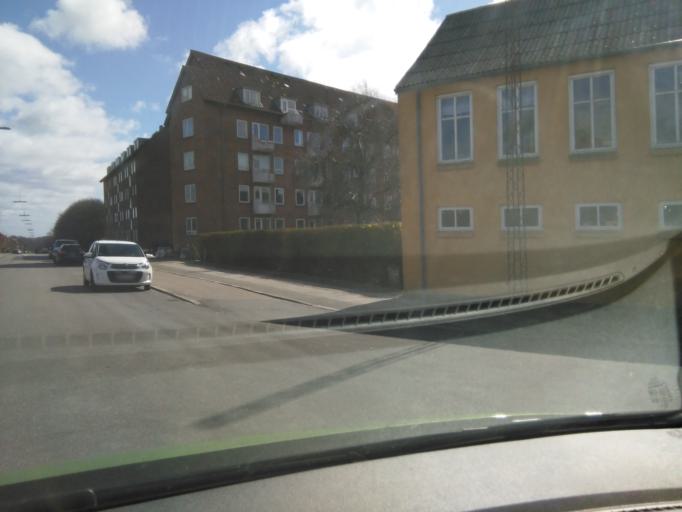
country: DK
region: Central Jutland
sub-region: Arhus Kommune
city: Arhus
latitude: 56.1764
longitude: 10.2040
